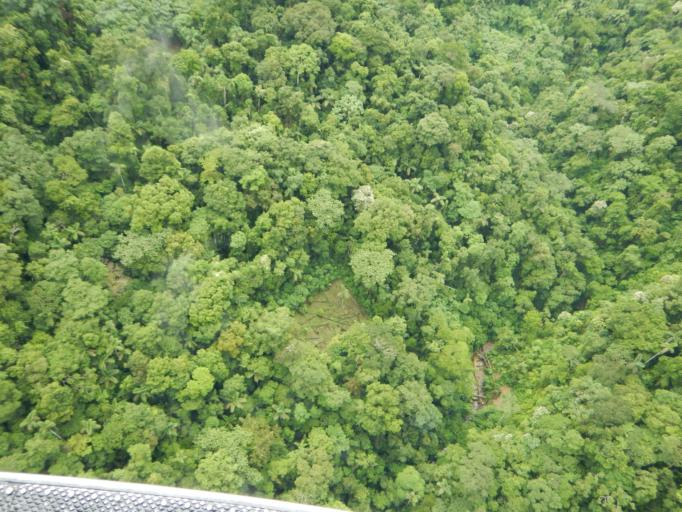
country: BO
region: Santa Cruz
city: Comarapa
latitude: -17.3833
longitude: -64.4639
